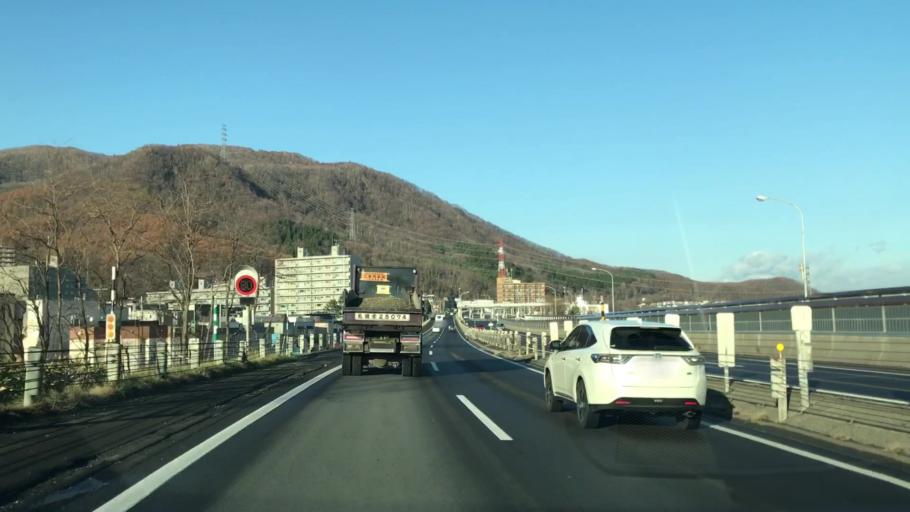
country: JP
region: Hokkaido
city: Sapporo
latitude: 43.0902
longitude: 141.2657
